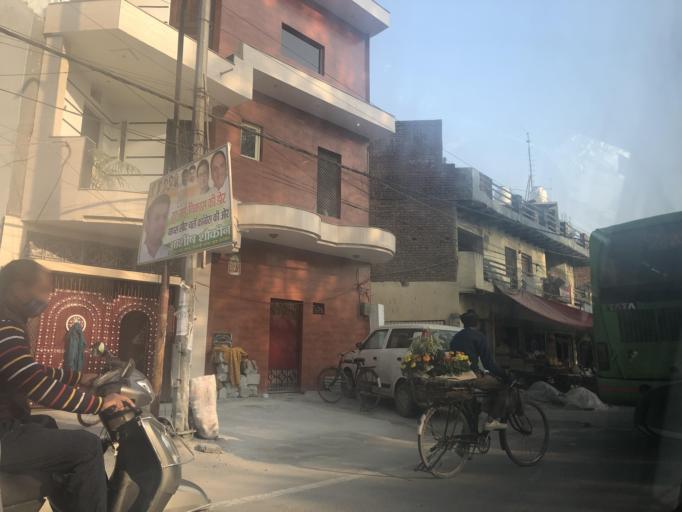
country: IN
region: Haryana
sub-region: Gurgaon
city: Gurgaon
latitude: 28.5599
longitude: 77.0031
